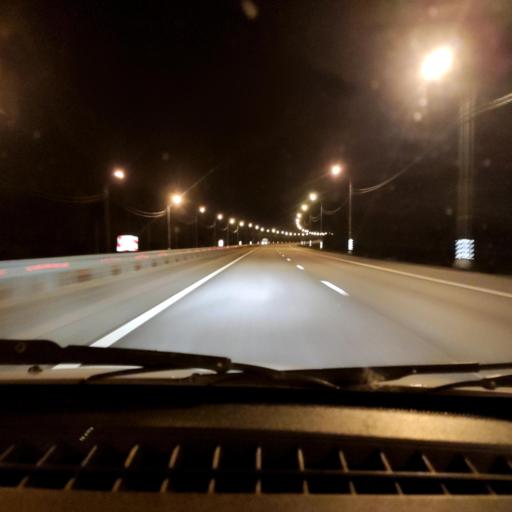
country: RU
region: Lipetsk
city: Zadonsk
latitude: 52.3776
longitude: 38.8867
